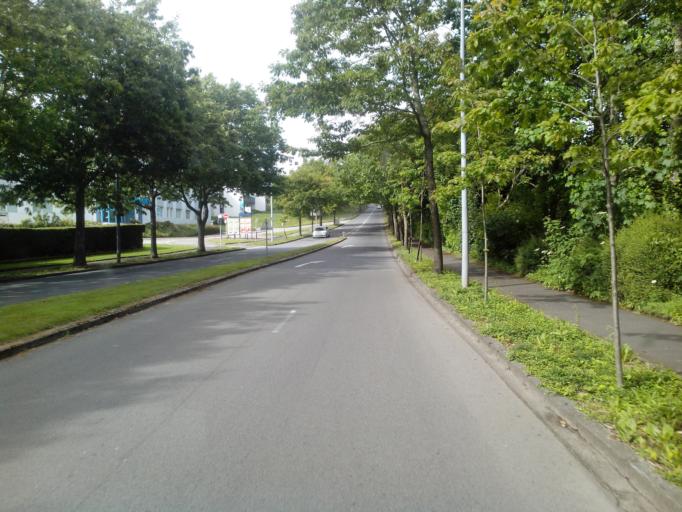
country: FR
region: Brittany
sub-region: Departement du Finistere
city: Brest
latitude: 48.4097
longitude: -4.4826
